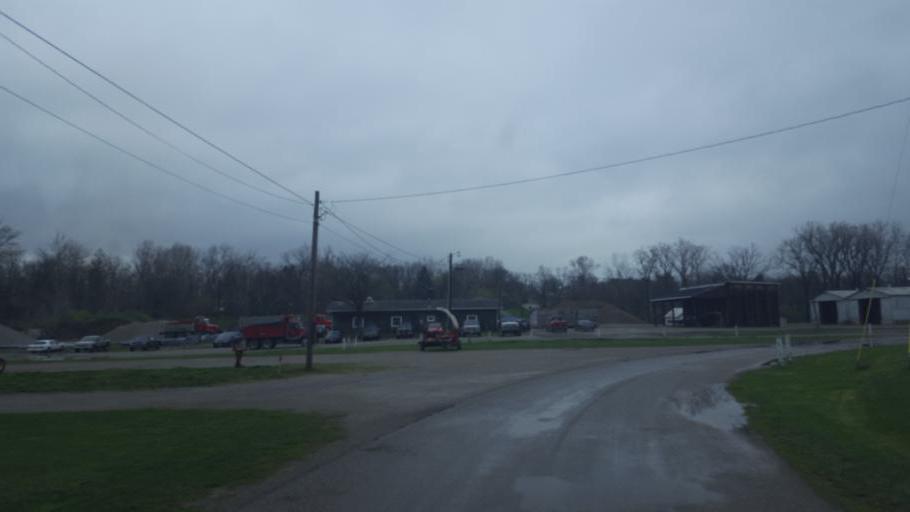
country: US
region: Ohio
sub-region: Morrow County
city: Mount Gilead
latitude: 40.5434
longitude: -82.8347
